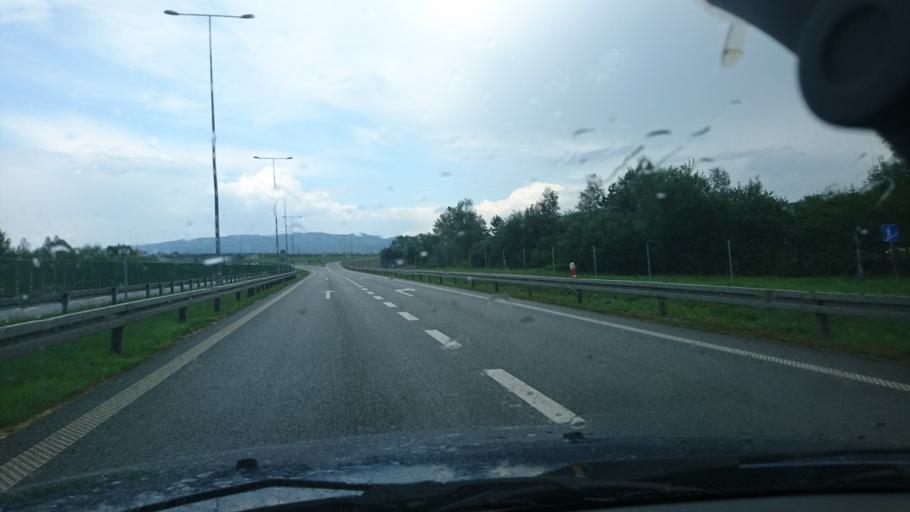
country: PL
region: Silesian Voivodeship
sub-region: Powiat zywiecki
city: Pietrzykowice
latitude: 49.6775
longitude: 19.1690
